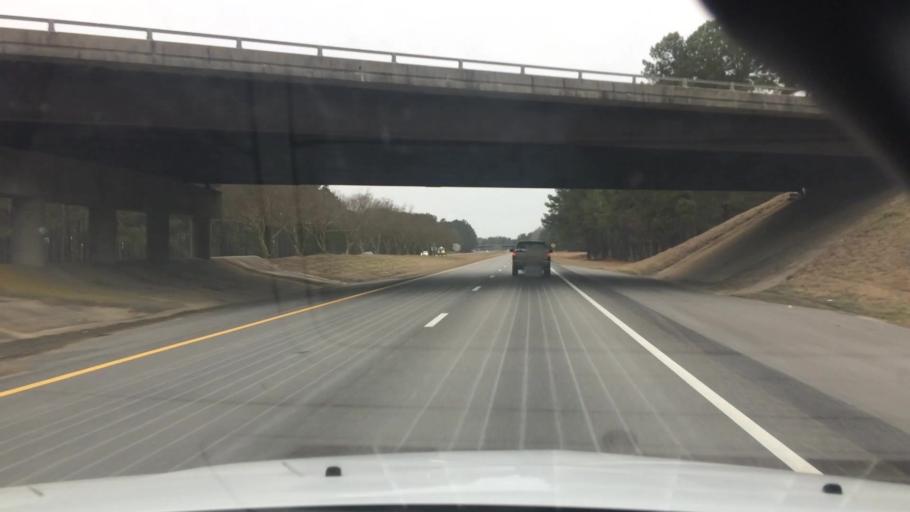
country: US
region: North Carolina
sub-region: Nash County
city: Spring Hope
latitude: 35.9317
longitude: -78.0973
